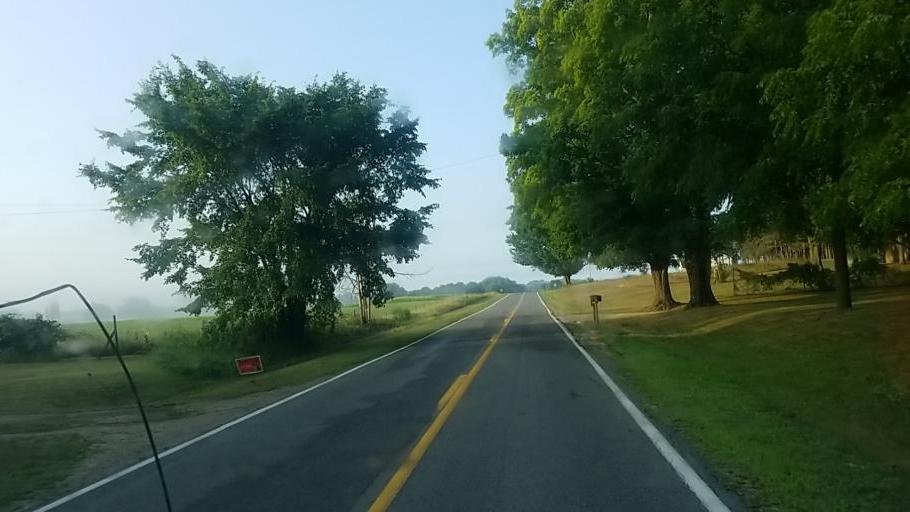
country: US
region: Michigan
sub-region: Muskegon County
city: Twin Lake
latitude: 43.4441
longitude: -86.0792
